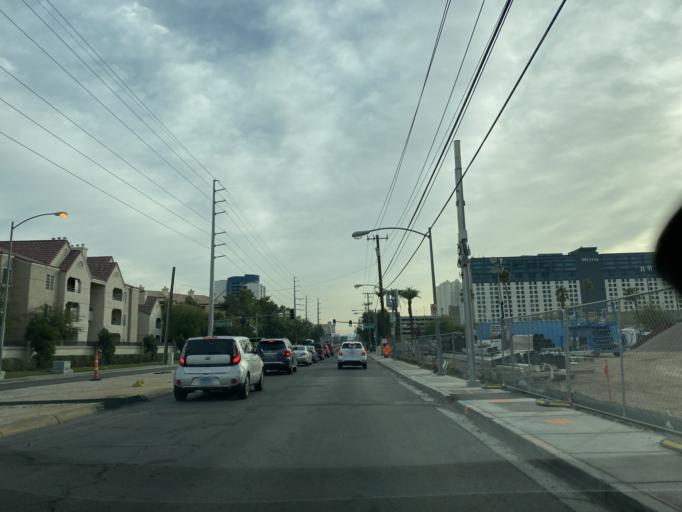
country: US
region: Nevada
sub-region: Clark County
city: Paradise
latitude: 36.1182
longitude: -115.1641
